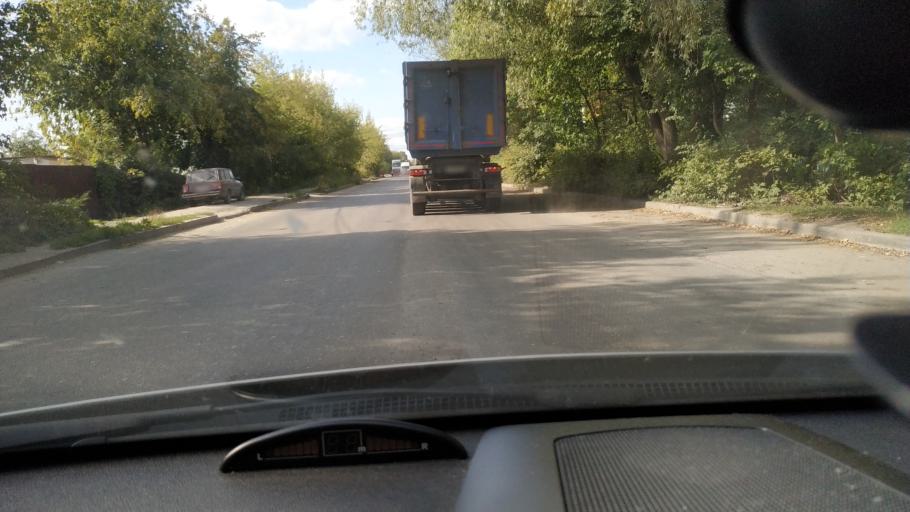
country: RU
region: Rjazan
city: Ryazan'
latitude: 54.6584
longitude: 39.6347
